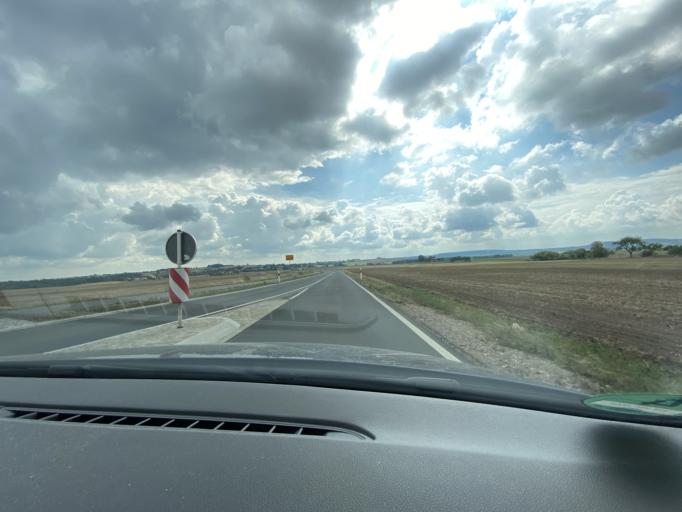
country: DE
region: Saxony
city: Tharandt
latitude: 51.0163
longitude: 13.5865
